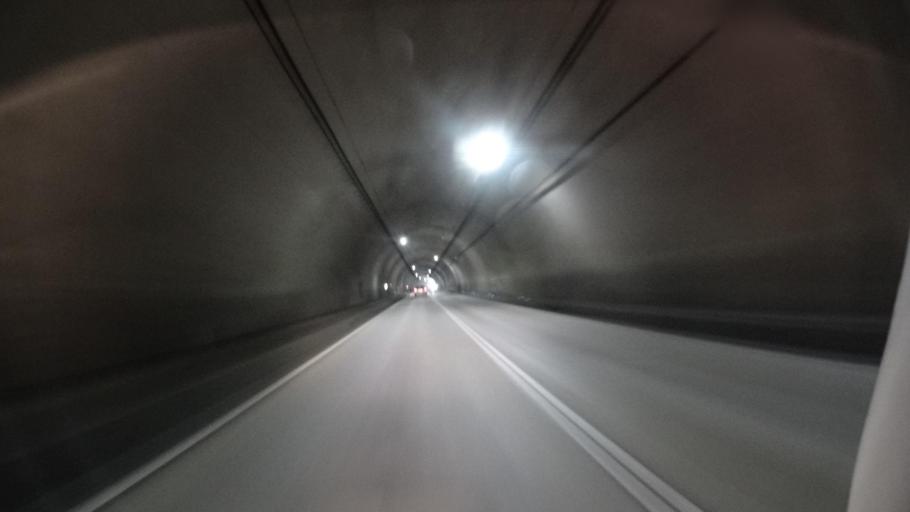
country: JP
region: Kyoto
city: Kameoka
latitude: 35.2250
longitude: 135.5727
